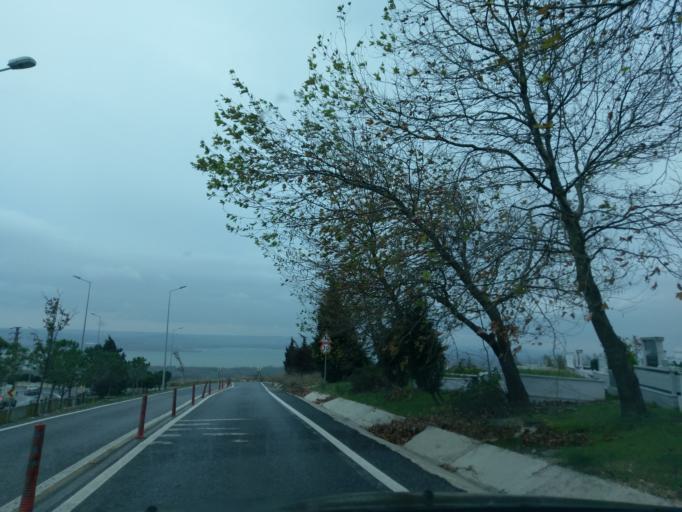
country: TR
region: Istanbul
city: Bueyuekcekmece
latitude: 41.0269
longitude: 28.6111
